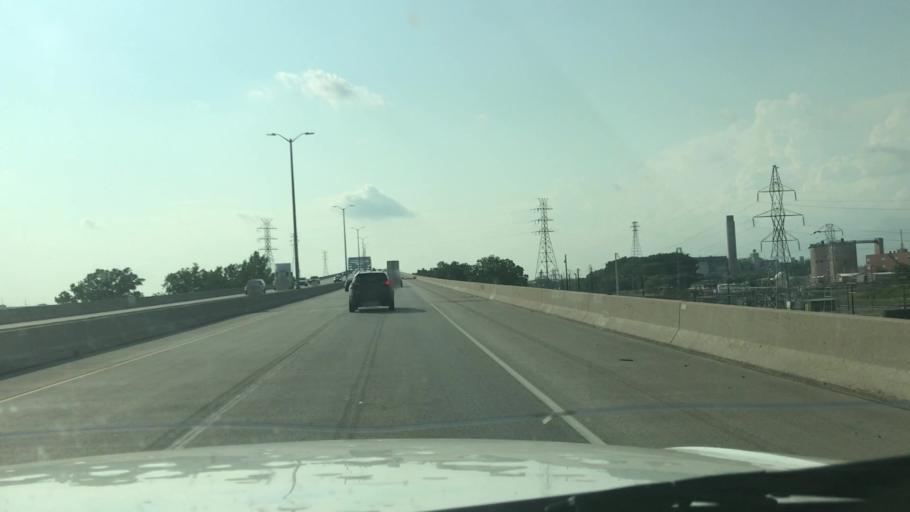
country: US
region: Wisconsin
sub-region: Brown County
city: Green Bay
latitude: 44.5292
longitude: -87.9945
